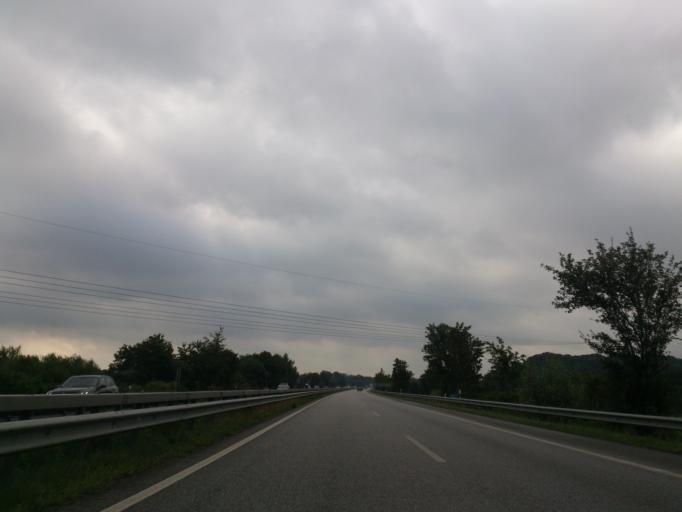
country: DE
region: Schleswig-Holstein
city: Hadenfeld
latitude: 54.0266
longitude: 9.4499
